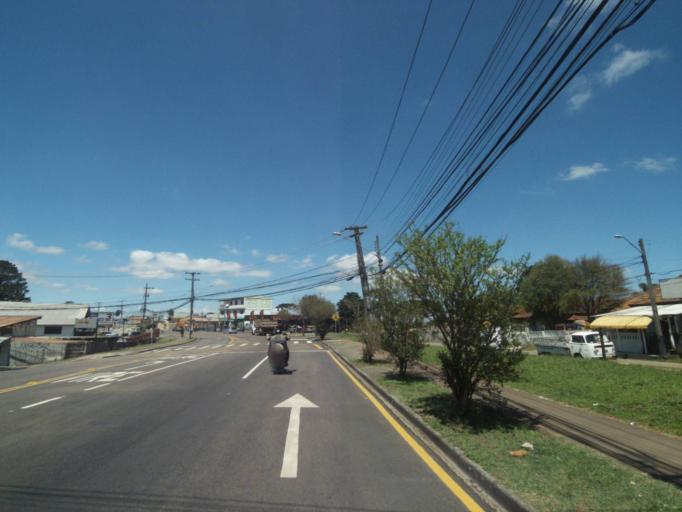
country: BR
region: Parana
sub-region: Curitiba
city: Curitiba
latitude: -25.3786
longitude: -49.2626
